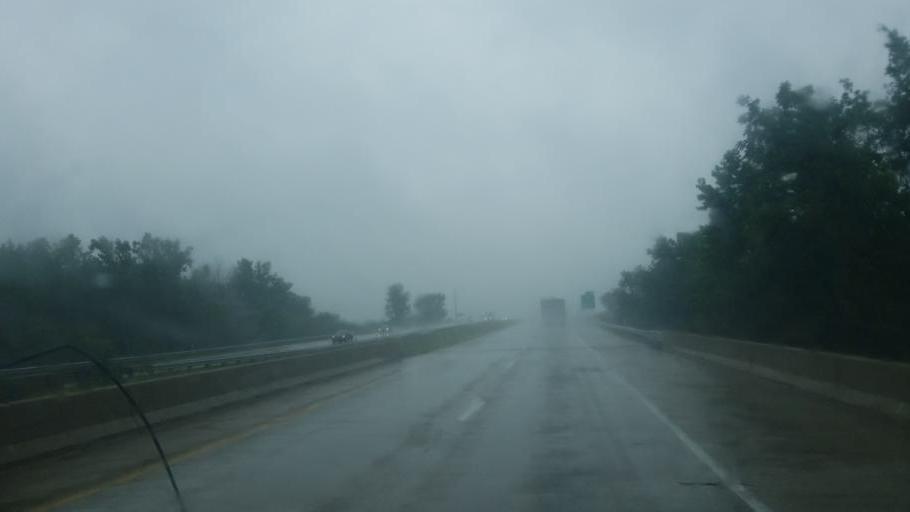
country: US
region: Indiana
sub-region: Delaware County
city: Yorktown
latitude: 40.2328
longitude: -85.5580
